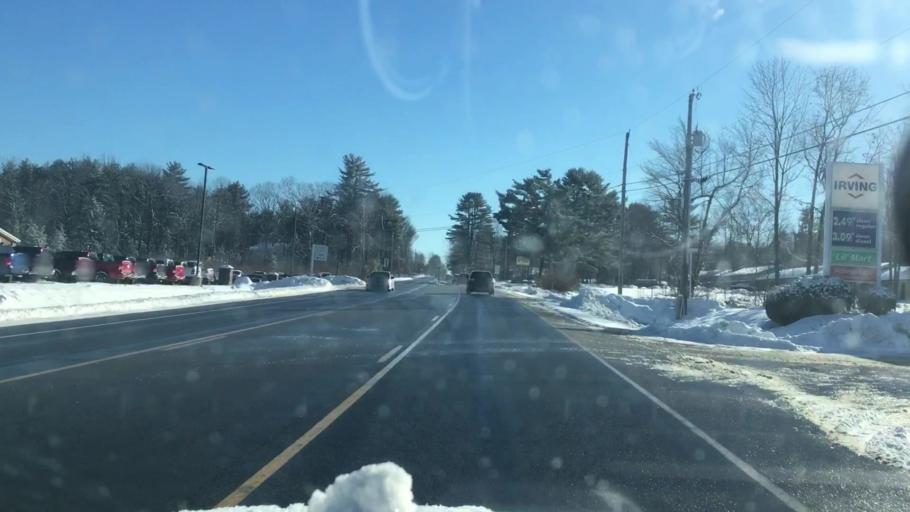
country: US
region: Maine
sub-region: Cumberland County
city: Bridgton
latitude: 44.0251
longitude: -70.6912
